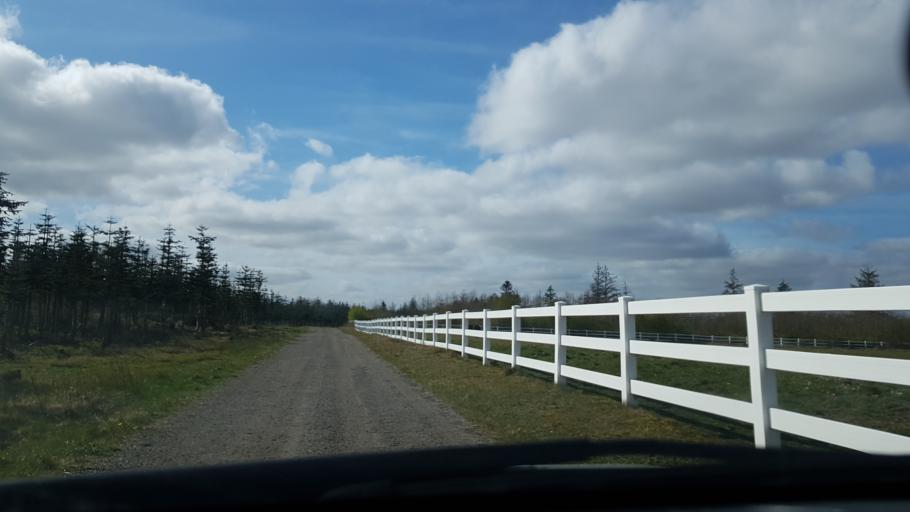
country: DK
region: South Denmark
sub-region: Haderslev Kommune
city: Gram
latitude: 55.2990
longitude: 8.9817
